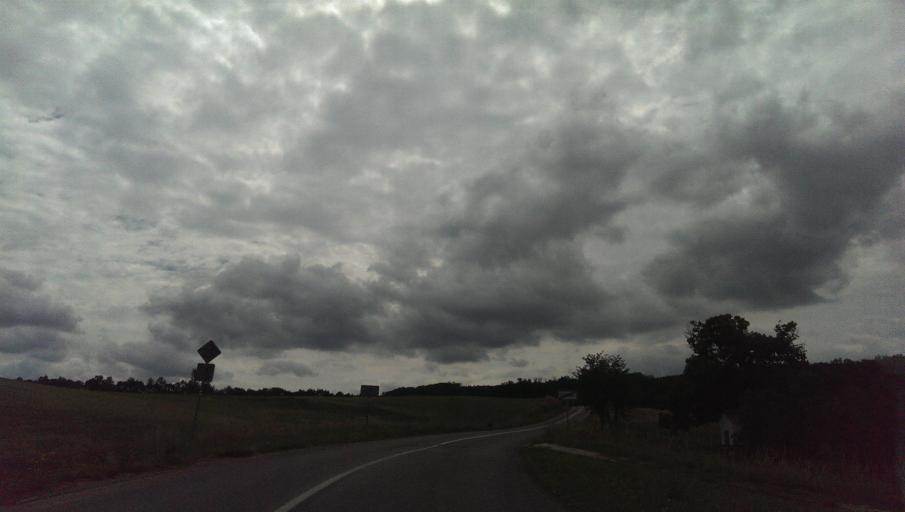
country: CZ
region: South Moravian
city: Velka nad Velickou
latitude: 48.9012
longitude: 17.5650
